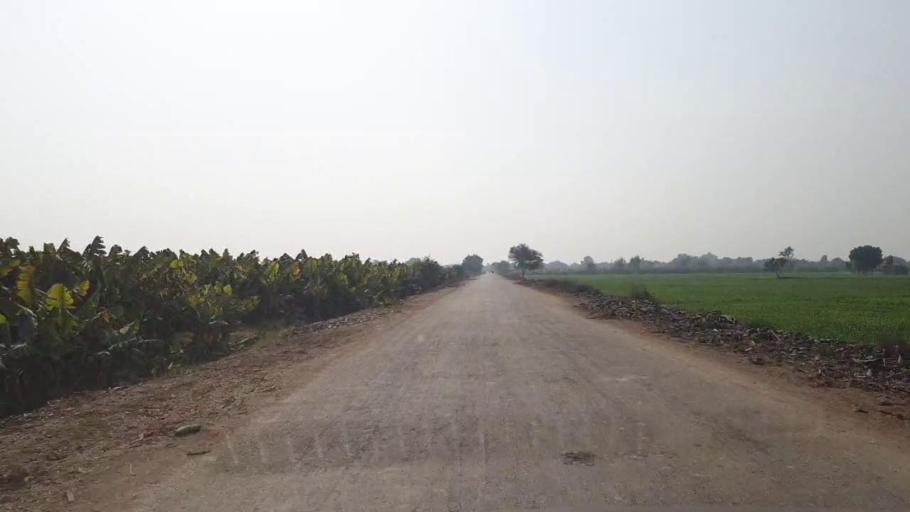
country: PK
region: Sindh
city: Hala
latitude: 25.8688
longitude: 68.4305
